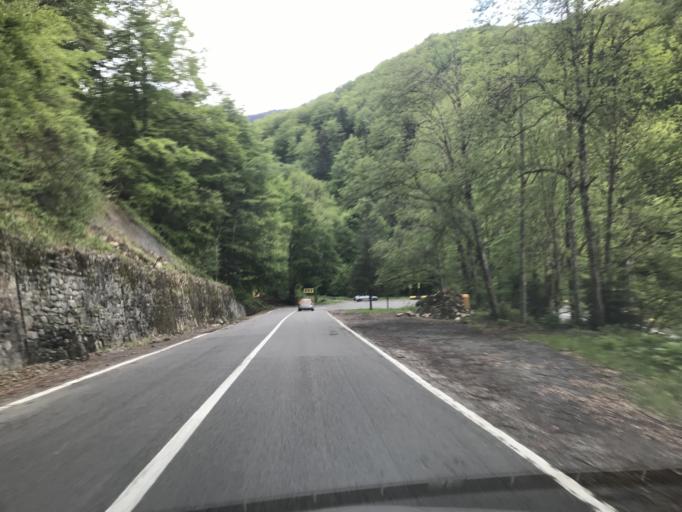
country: RO
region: Sibiu
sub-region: Comuna Cartisoara
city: Cartisoara
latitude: 45.6684
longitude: 24.5777
